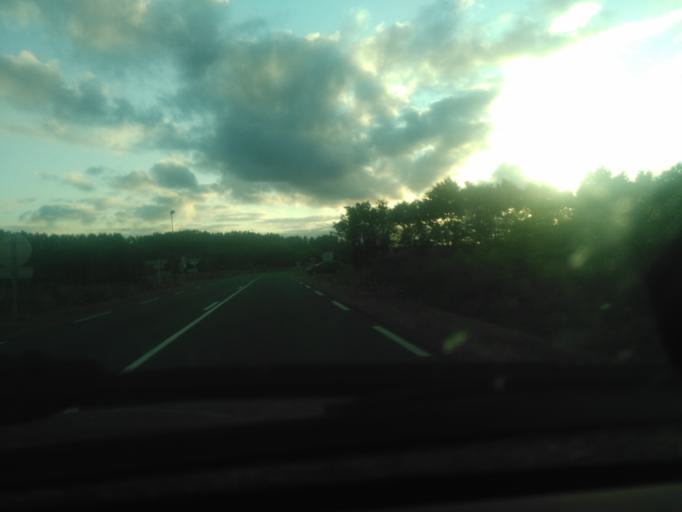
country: FR
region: Pays de la Loire
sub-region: Departement de la Vendee
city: La Ferriere
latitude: 46.7068
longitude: -1.3204
